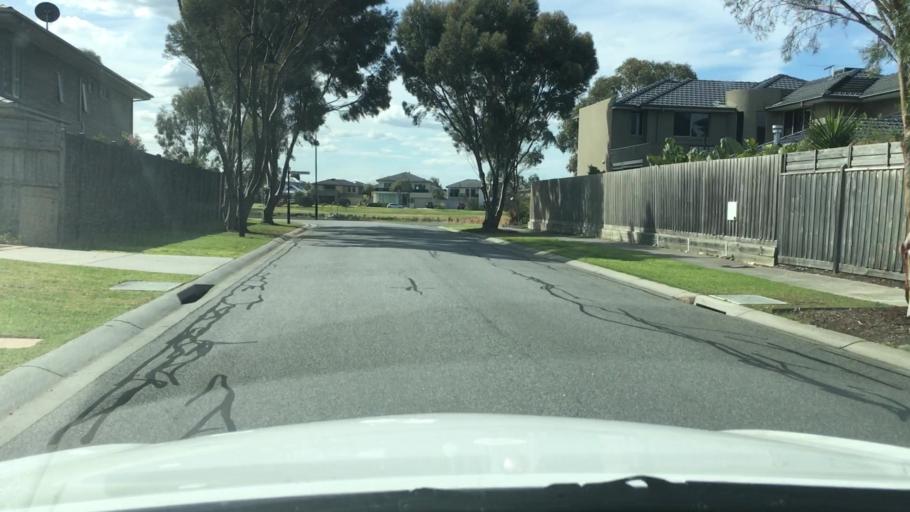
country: AU
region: Victoria
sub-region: Kingston
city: Waterways
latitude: -38.0164
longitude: 145.1318
